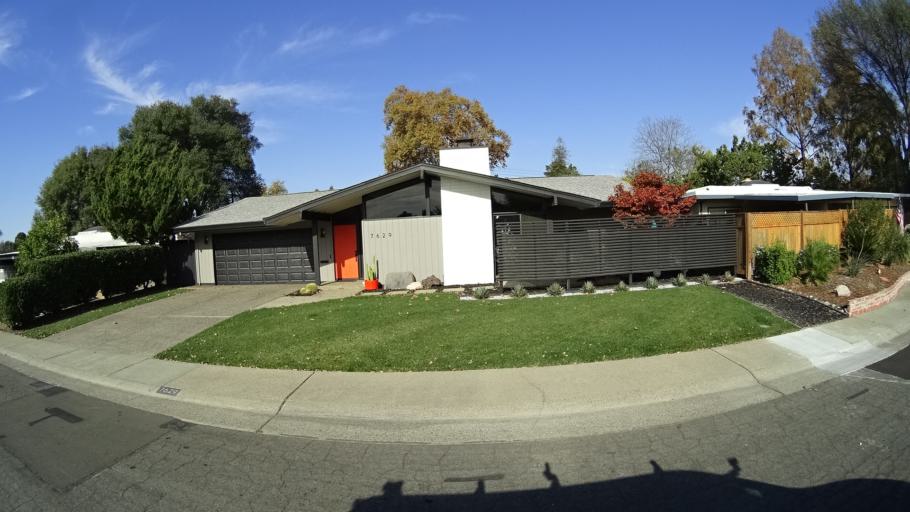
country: US
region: California
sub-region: Sacramento County
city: Fair Oaks
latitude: 38.6688
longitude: -121.2825
